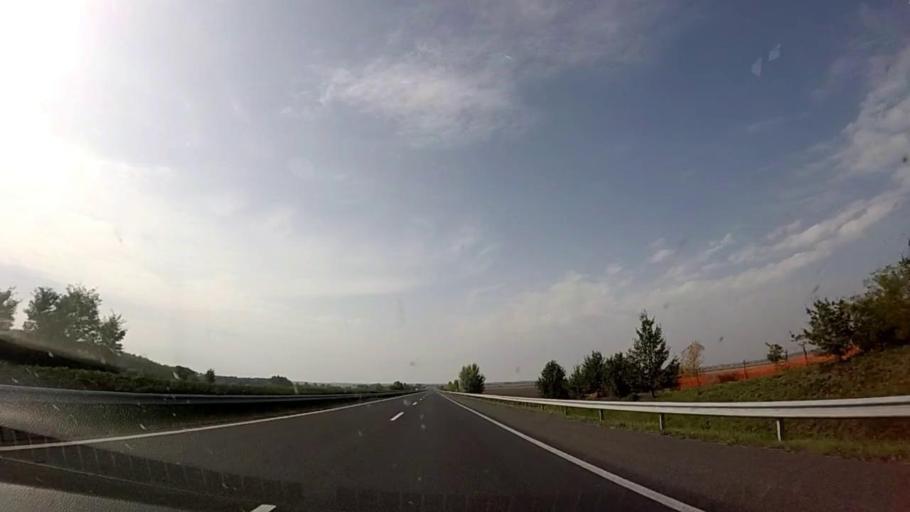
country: HU
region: Zala
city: Becsehely
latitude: 46.4333
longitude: 16.7944
